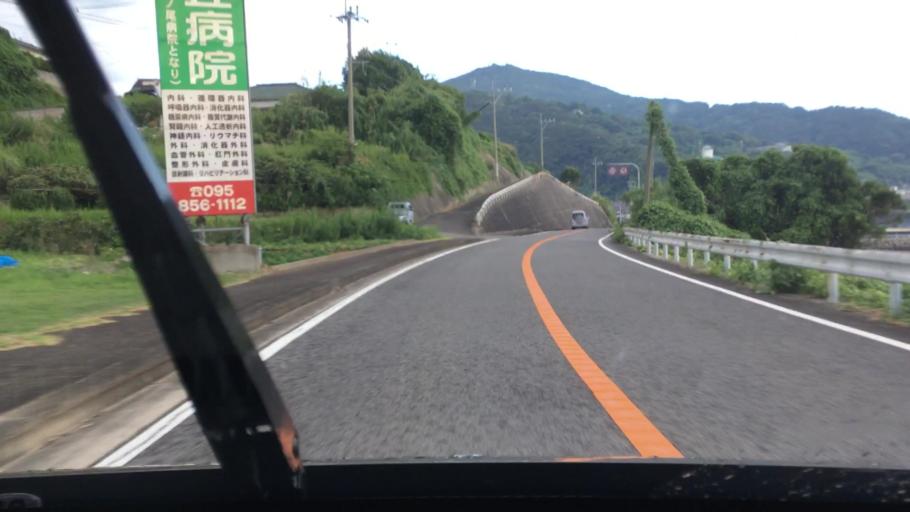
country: JP
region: Nagasaki
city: Togitsu
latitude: 32.8840
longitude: 129.6783
